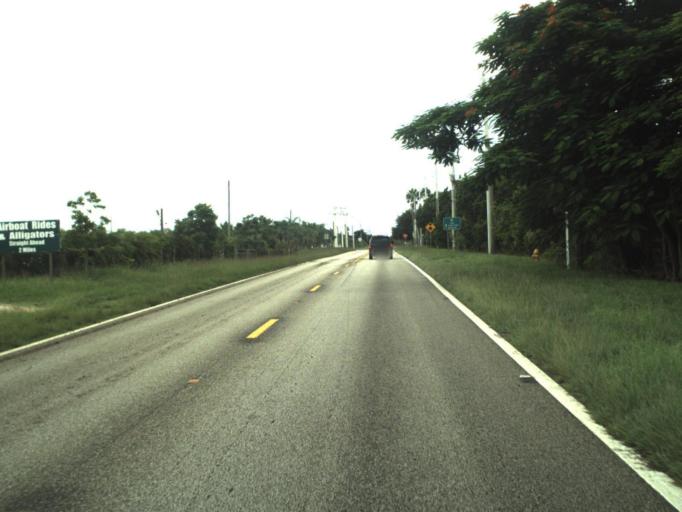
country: US
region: Florida
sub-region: Miami-Dade County
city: Florida City
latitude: 25.4206
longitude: -80.5014
